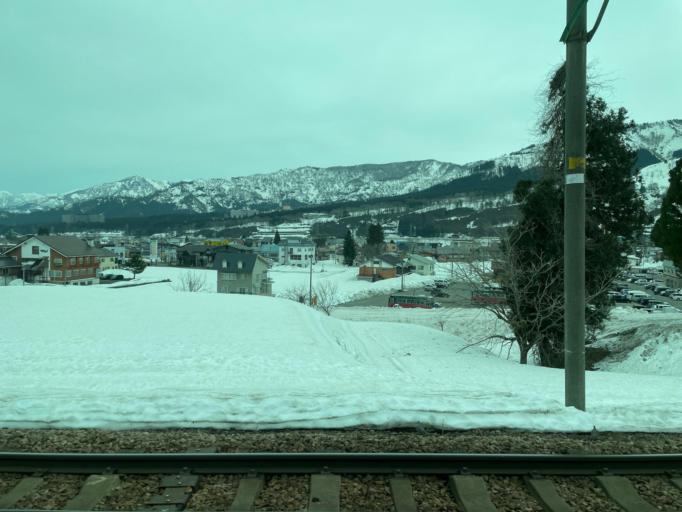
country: JP
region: Niigata
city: Shiozawa
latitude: 36.9806
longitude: 138.8004
